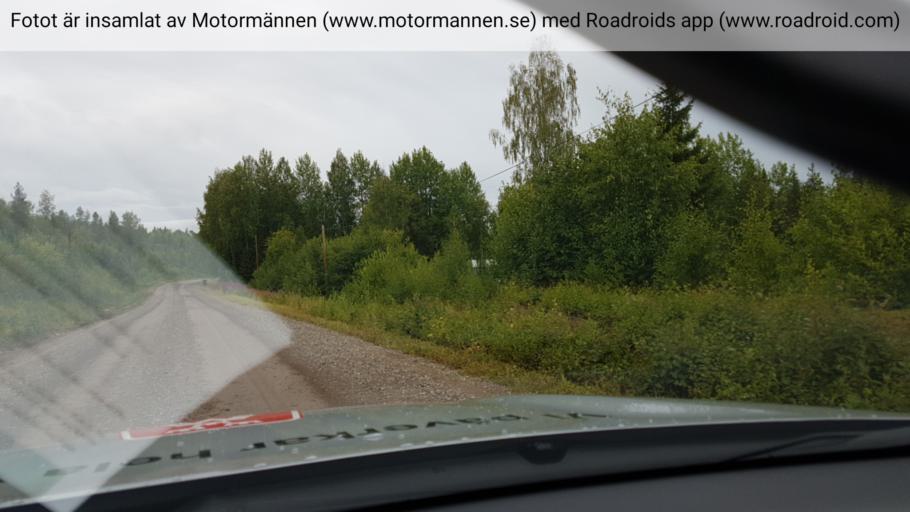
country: SE
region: Norrbotten
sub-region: Alvsbyns Kommun
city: AElvsbyn
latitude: 66.0049
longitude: 21.1228
